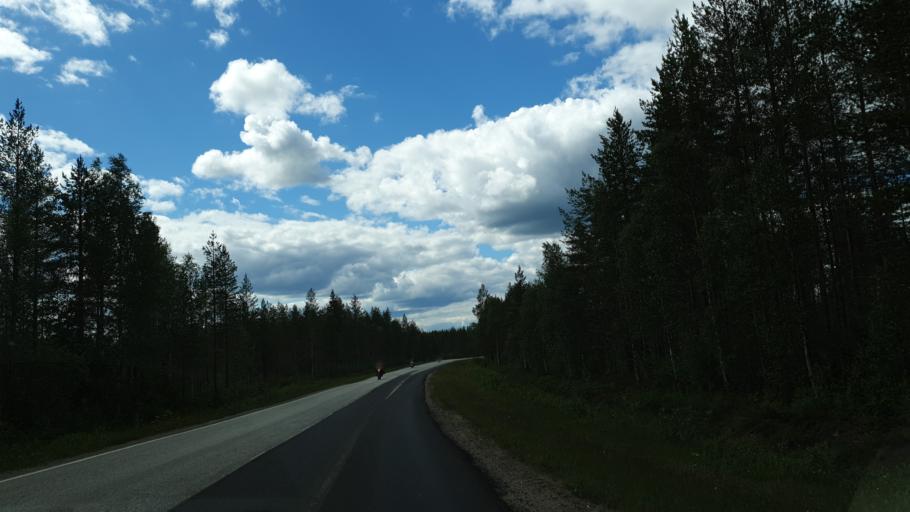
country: FI
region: Kainuu
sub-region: Kehys-Kainuu
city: Kuhmo
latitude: 63.9423
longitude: 29.6107
